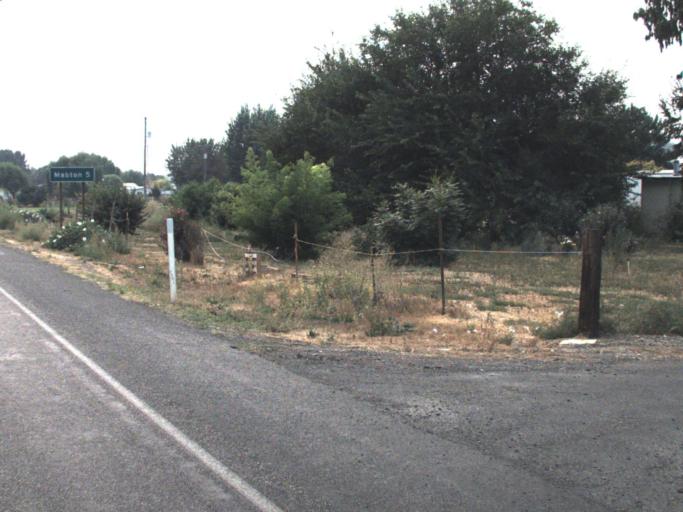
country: US
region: Washington
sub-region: Yakima County
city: Sunnyside
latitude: 46.2844
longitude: -119.9992
